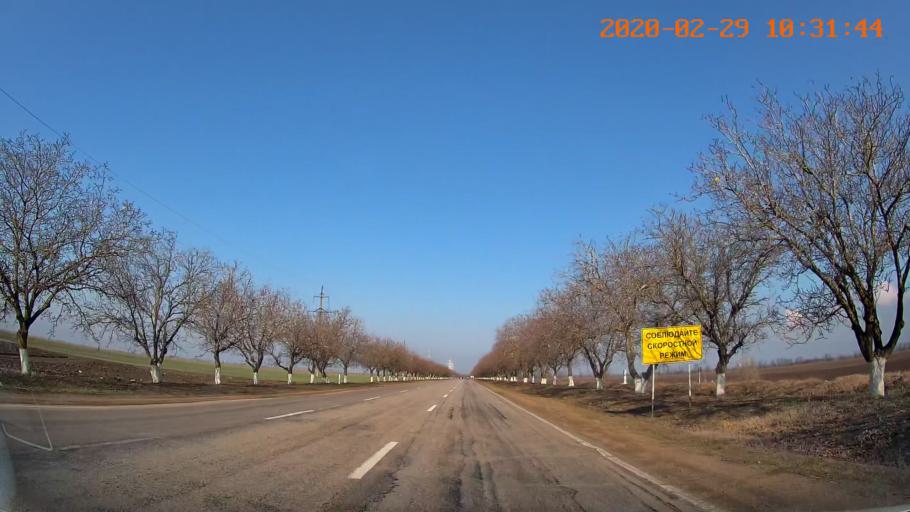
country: UA
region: Odessa
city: Velykoploske
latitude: 46.9522
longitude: 29.5606
